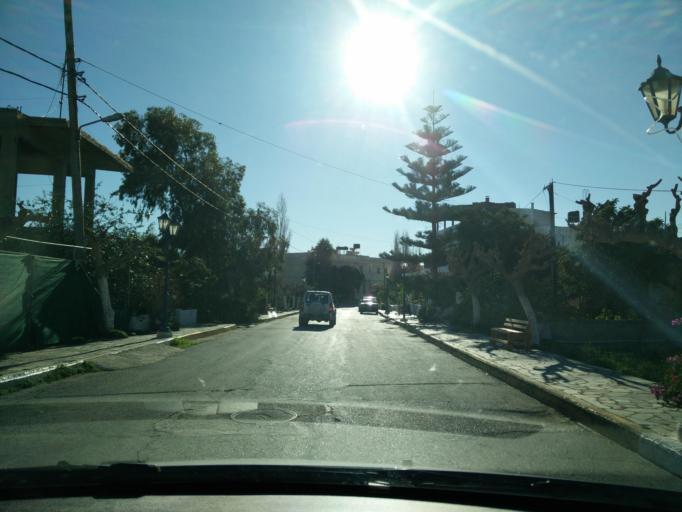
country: GR
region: Crete
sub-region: Nomos Lasithiou
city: Gra Liyia
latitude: 35.0047
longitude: 25.5862
